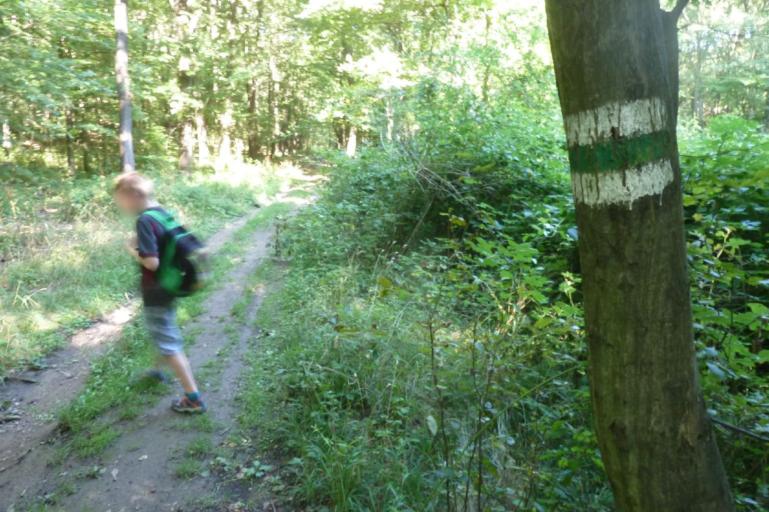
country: HU
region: Pest
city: Kismaros
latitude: 47.8945
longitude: 18.9668
